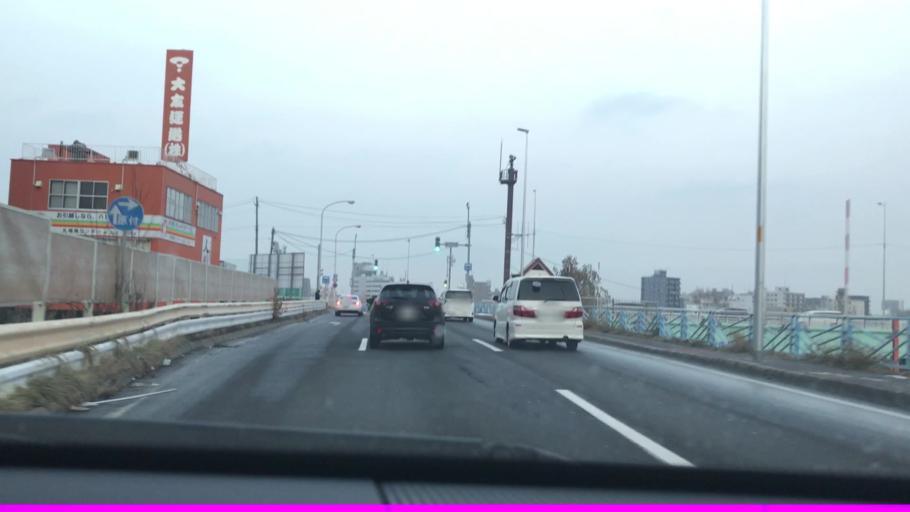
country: JP
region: Hokkaido
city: Sapporo
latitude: 43.0296
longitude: 141.3533
